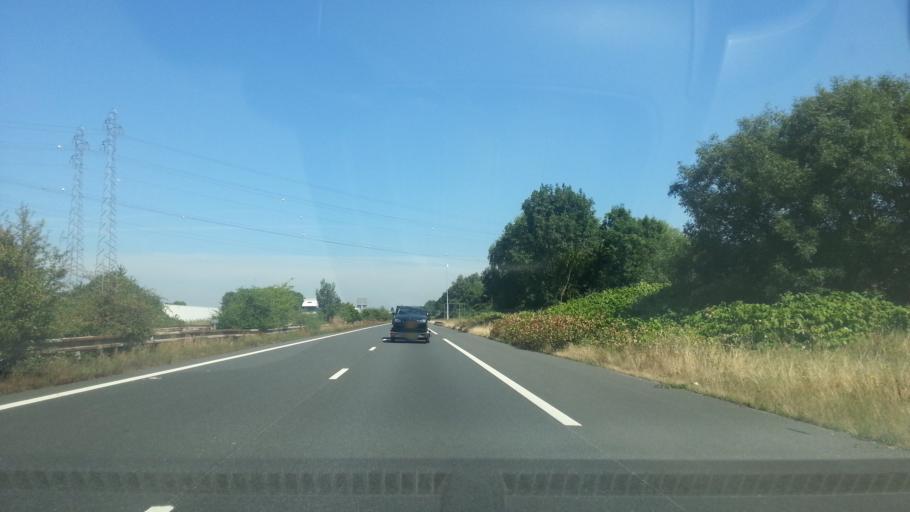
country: FR
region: Ile-de-France
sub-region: Departement de l'Essonne
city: Orsay
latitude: 48.6758
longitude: 2.2010
